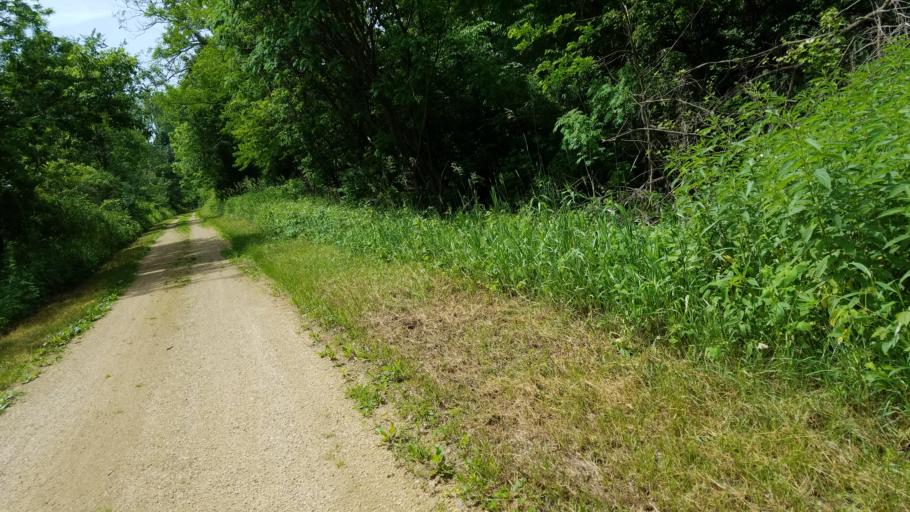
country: US
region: Wisconsin
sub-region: Dunn County
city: Menomonie
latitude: 44.8001
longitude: -91.9471
